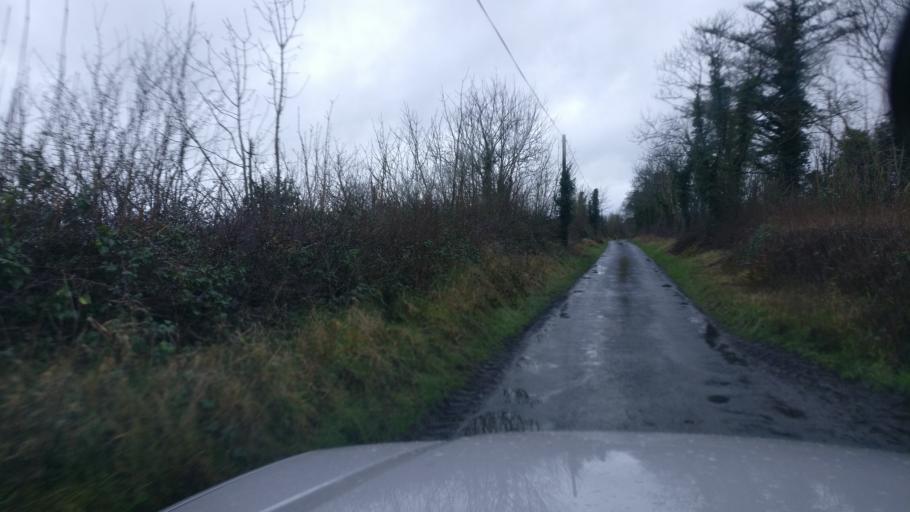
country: IE
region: Connaught
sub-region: County Galway
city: Ballinasloe
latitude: 53.2517
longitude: -8.3449
